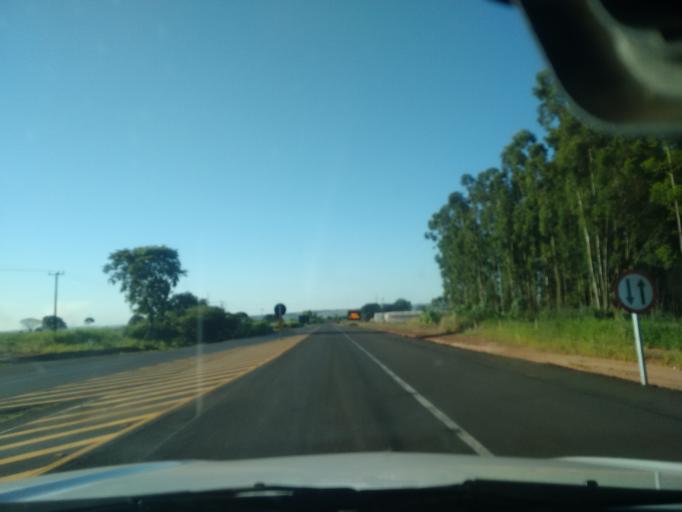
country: BR
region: Mato Grosso do Sul
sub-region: Eldorado
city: Eldorado
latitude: -23.8641
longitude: -54.3305
